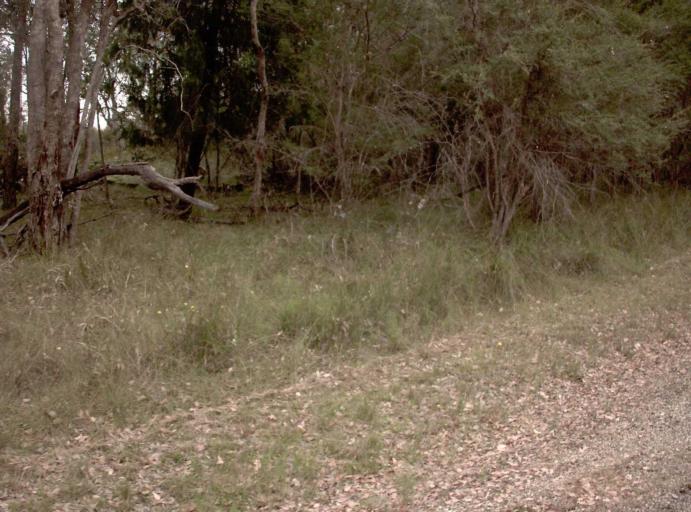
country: AU
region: Victoria
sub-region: East Gippsland
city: Bairnsdale
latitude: -37.7139
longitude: 147.3136
